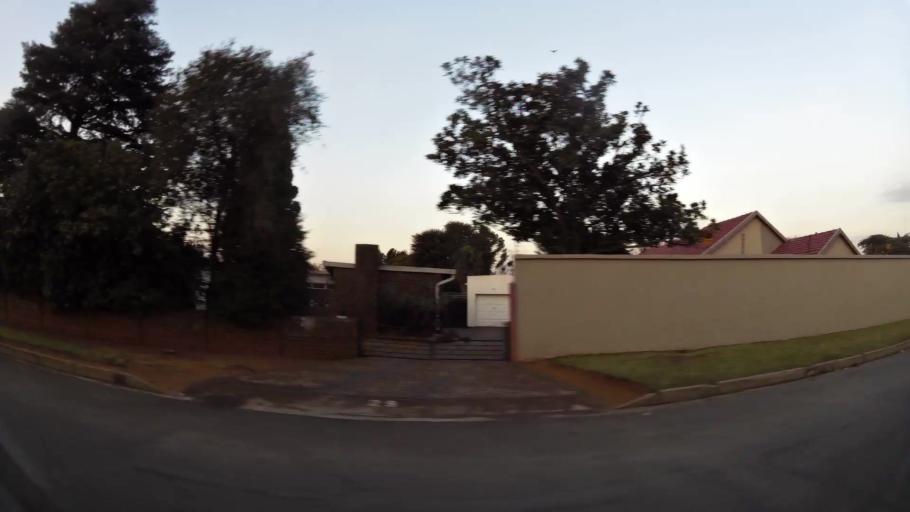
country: ZA
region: Gauteng
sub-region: Ekurhuleni Metropolitan Municipality
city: Tembisa
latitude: -26.0577
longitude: 28.2406
